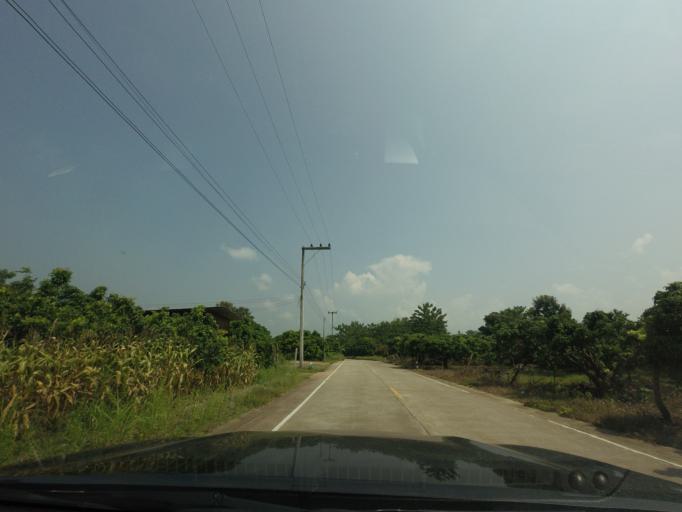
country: TH
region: Nan
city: Nan
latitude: 18.8572
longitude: 100.8059
